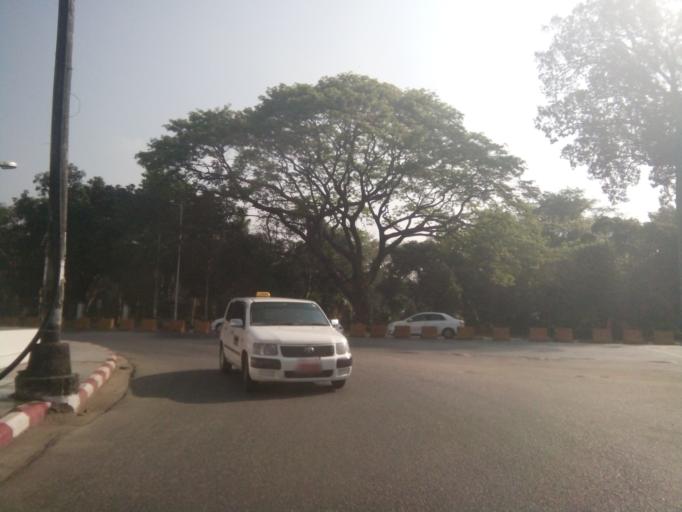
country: MM
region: Yangon
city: Yangon
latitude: 16.8216
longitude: 96.1318
